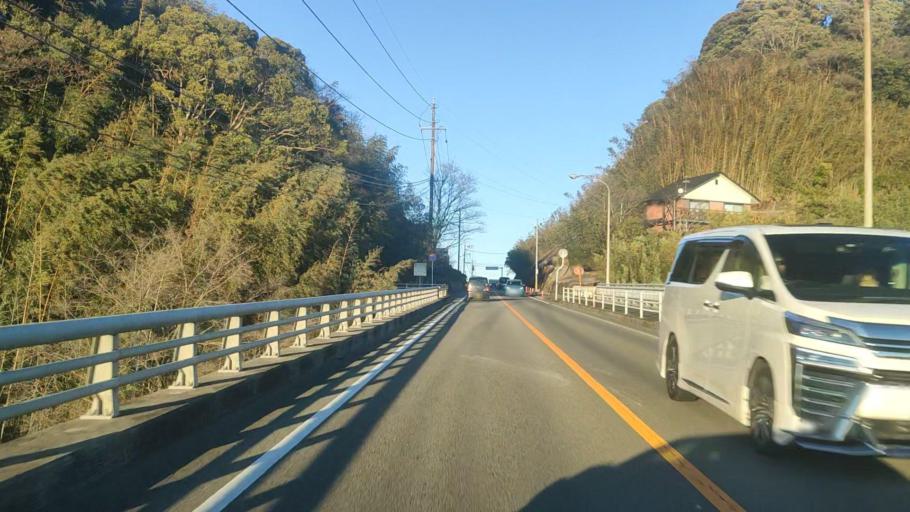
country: JP
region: Miyazaki
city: Miyazaki-shi
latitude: 31.8633
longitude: 131.3873
